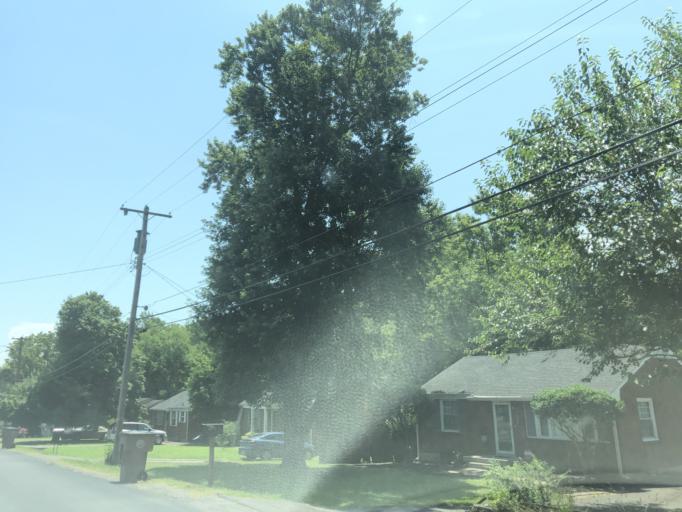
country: US
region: Tennessee
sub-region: Davidson County
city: Lakewood
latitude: 36.1535
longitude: -86.6549
